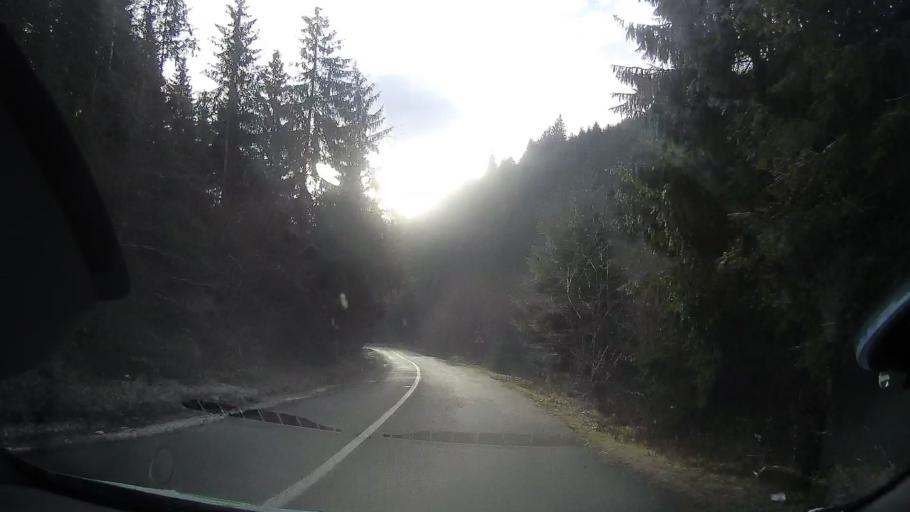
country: RO
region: Alba
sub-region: Comuna Albac
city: Albac
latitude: 46.4743
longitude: 22.9631
